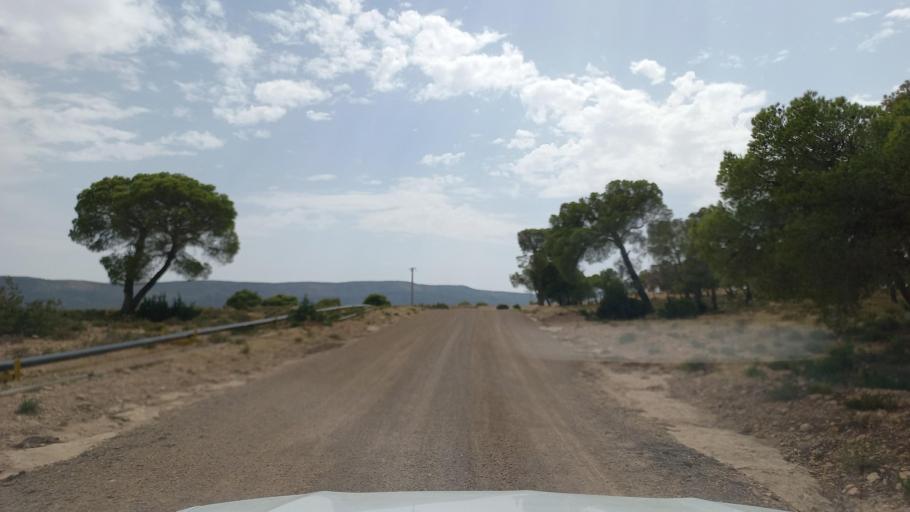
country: TN
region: Al Qasrayn
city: Kasserine
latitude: 35.3795
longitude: 8.8795
